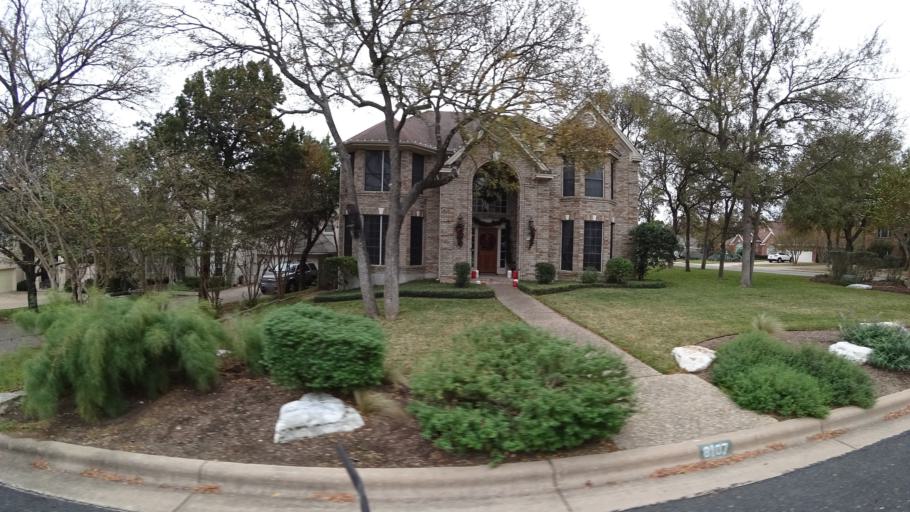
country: US
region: Texas
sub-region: Williamson County
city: Jollyville
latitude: 30.3899
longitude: -97.8014
